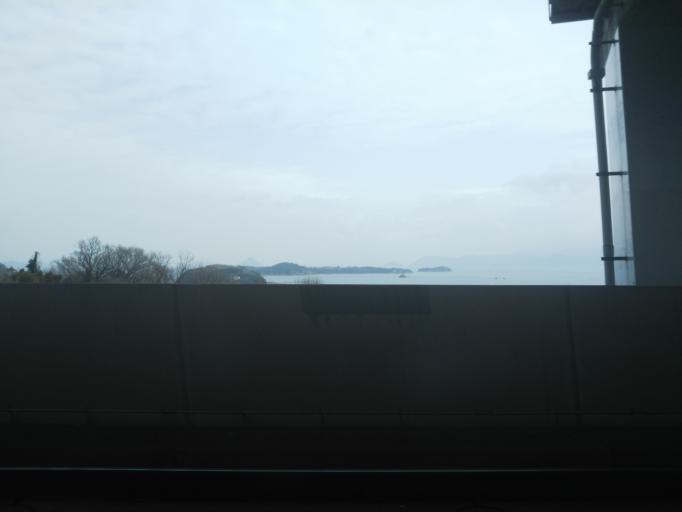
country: JP
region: Kagawa
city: Sakaidecho
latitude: 34.4254
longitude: 133.8046
